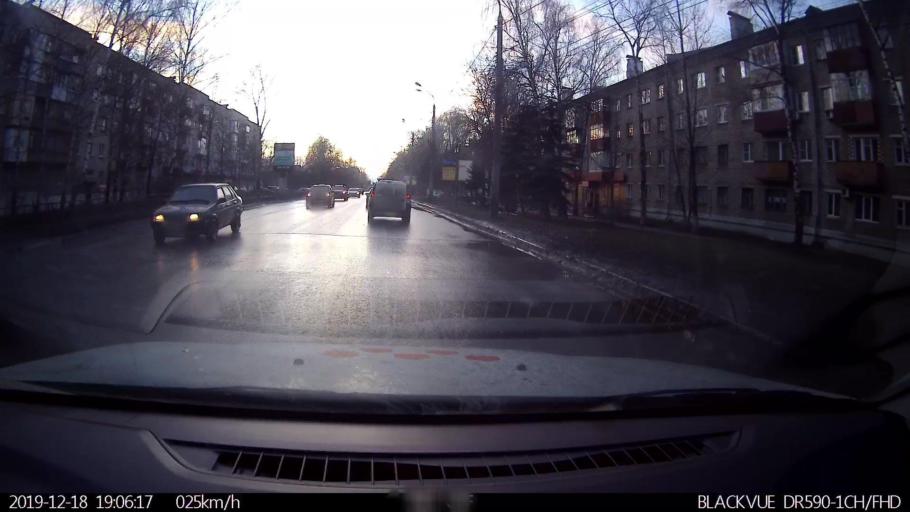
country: RU
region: Nizjnij Novgorod
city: Nizhniy Novgorod
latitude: 56.3230
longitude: 43.8662
